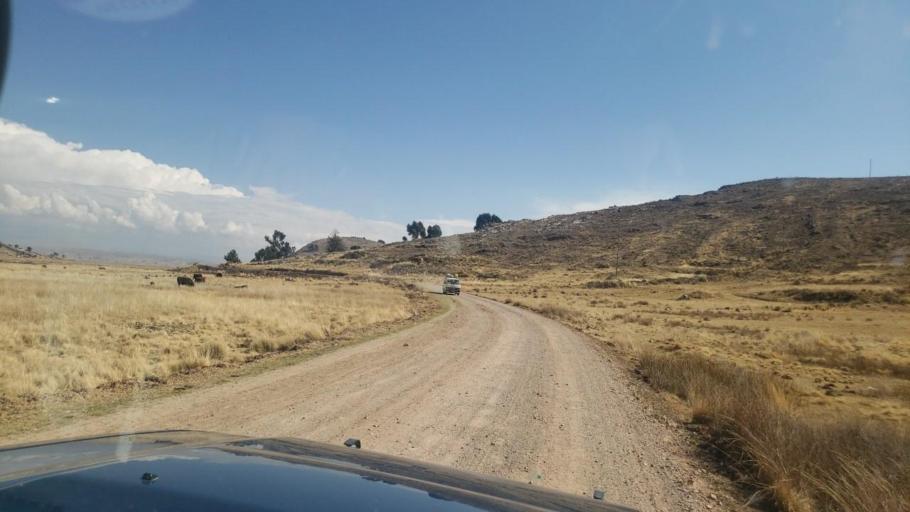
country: BO
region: La Paz
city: Huatajata
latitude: -16.3362
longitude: -68.6816
